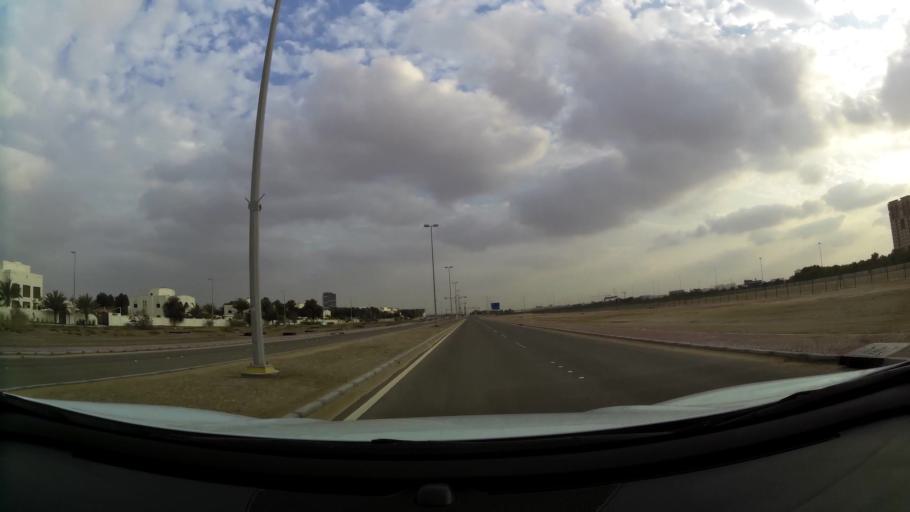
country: AE
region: Abu Dhabi
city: Abu Dhabi
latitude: 24.3862
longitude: 54.5270
